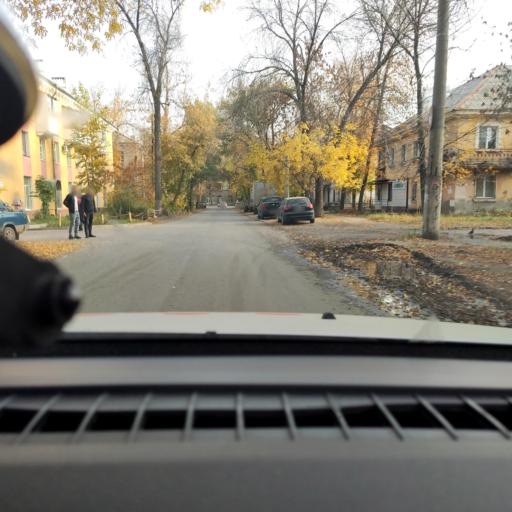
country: RU
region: Samara
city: Samara
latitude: 53.1177
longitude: 50.0794
